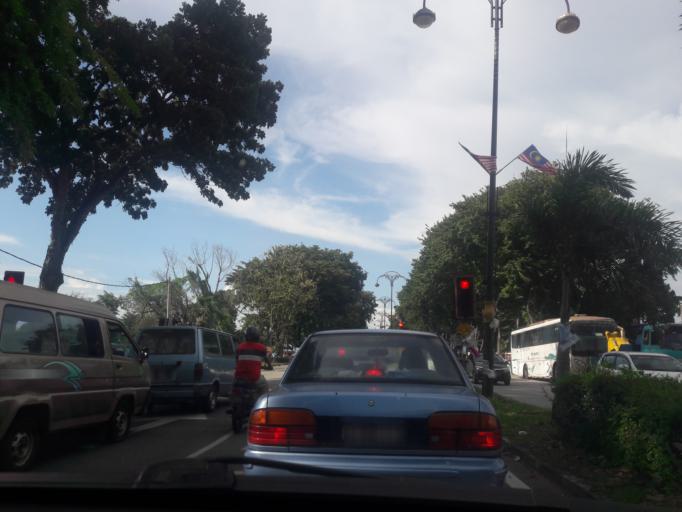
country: MY
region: Kedah
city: Sungai Petani
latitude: 5.6525
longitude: 100.5001
